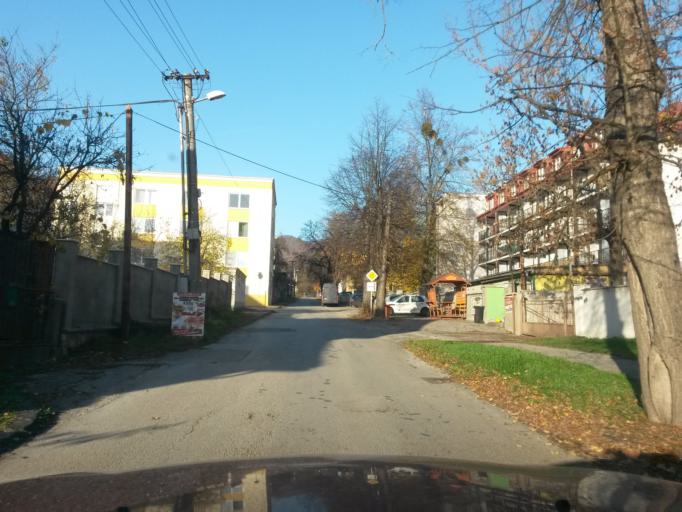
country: SK
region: Kosicky
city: Roznava
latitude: 48.6611
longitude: 20.5275
